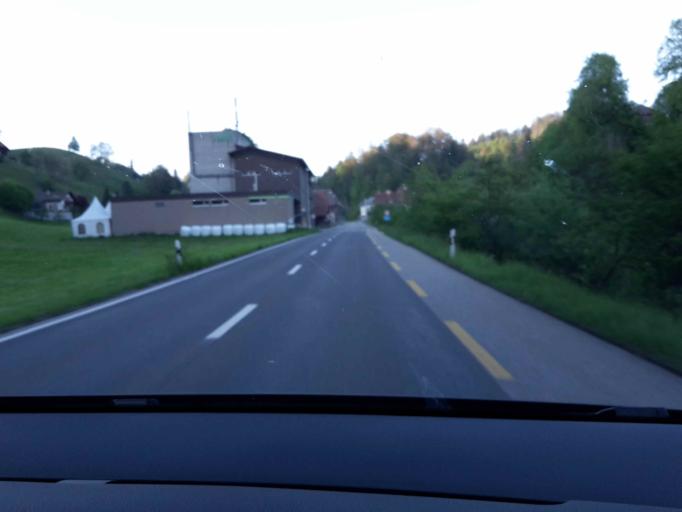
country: CH
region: Bern
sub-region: Emmental District
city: Lutzelfluh
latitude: 47.0326
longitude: 7.6874
